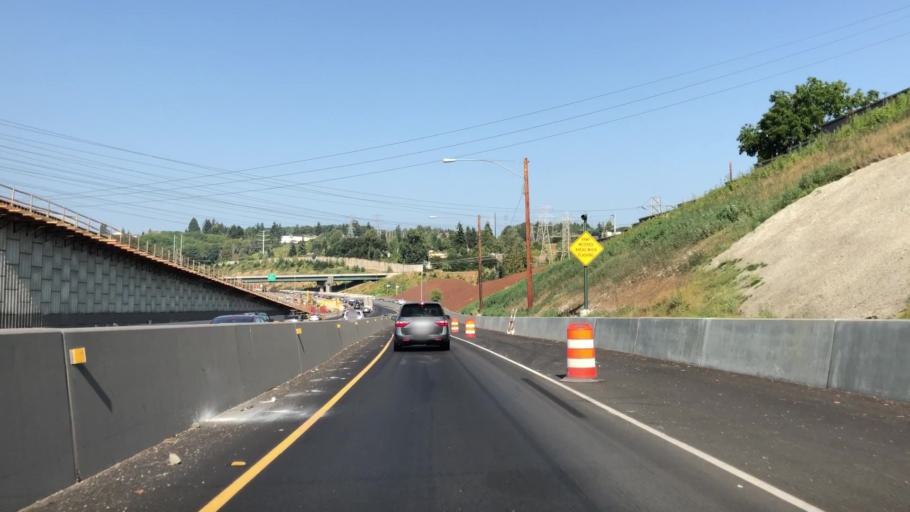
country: US
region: Washington
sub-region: King County
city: Renton
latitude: 47.4678
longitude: -122.2137
